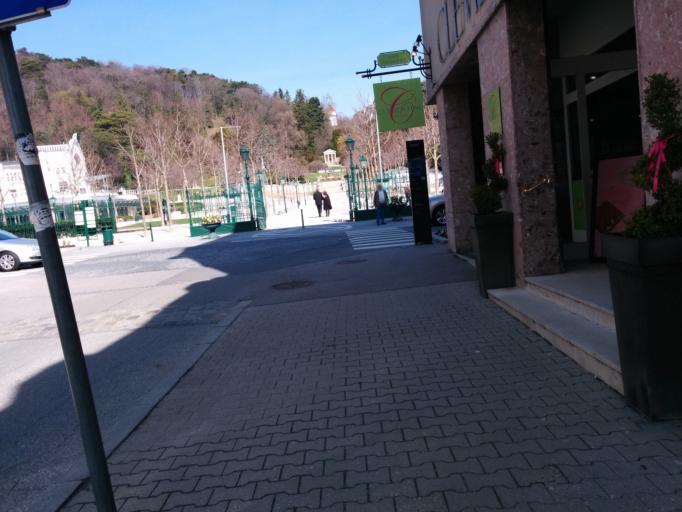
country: AT
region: Lower Austria
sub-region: Politischer Bezirk Baden
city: Baden
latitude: 48.0097
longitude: 16.2337
